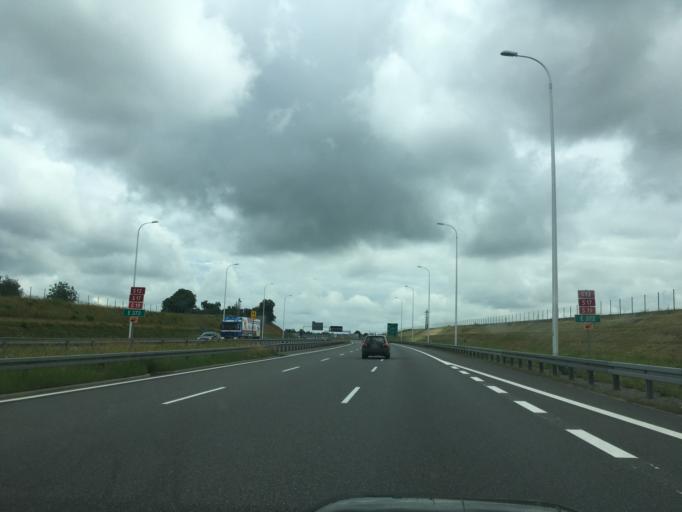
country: PL
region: Lublin Voivodeship
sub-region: Powiat lubelski
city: Lublin
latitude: 51.2986
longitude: 22.5231
